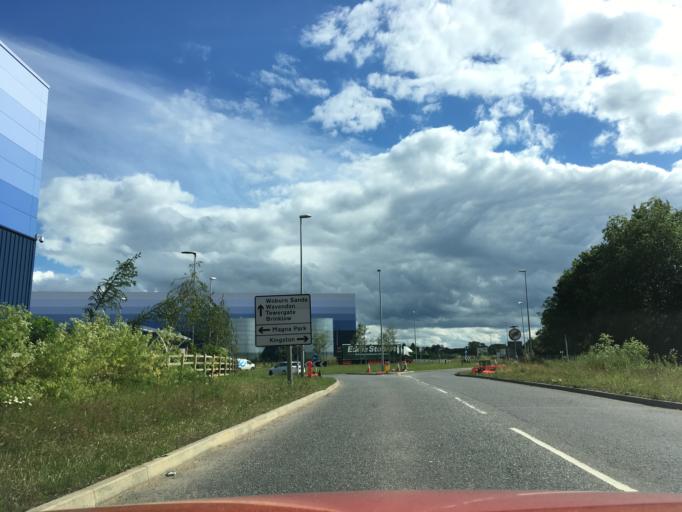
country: GB
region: England
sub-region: Milton Keynes
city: Wavendon
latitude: 52.0375
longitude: -0.6761
